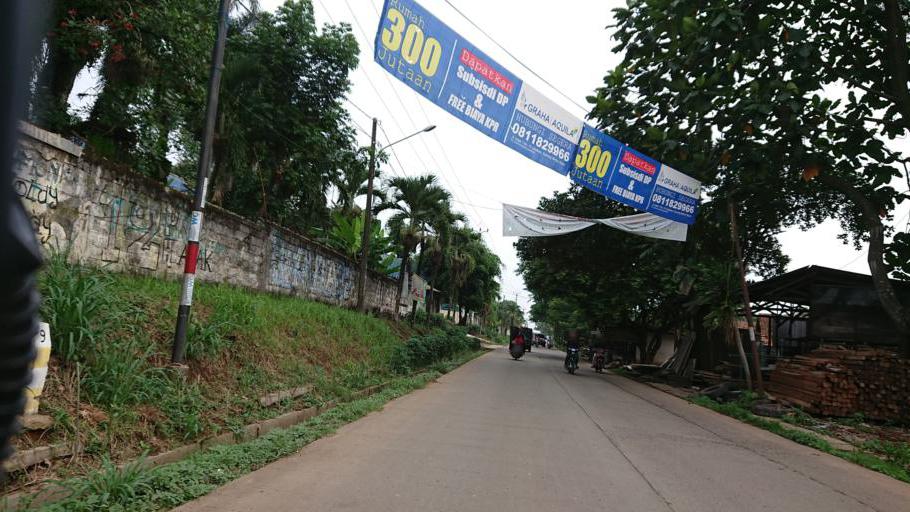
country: ID
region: West Java
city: Parung
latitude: -6.4000
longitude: 106.6892
